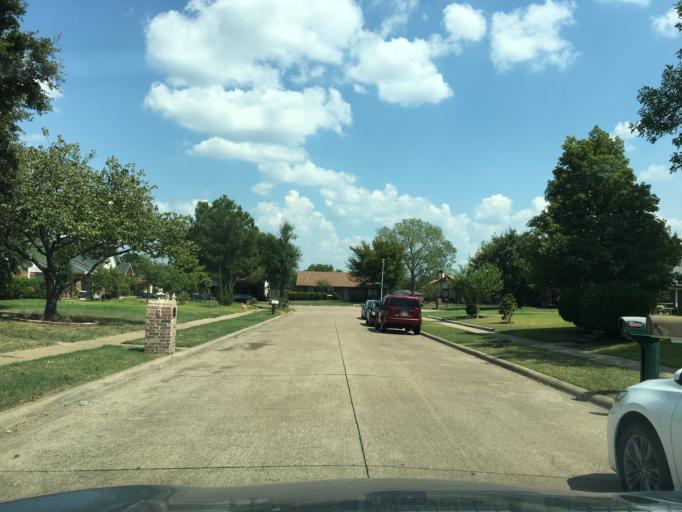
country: US
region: Texas
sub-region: Dallas County
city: Garland
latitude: 32.9464
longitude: -96.6637
